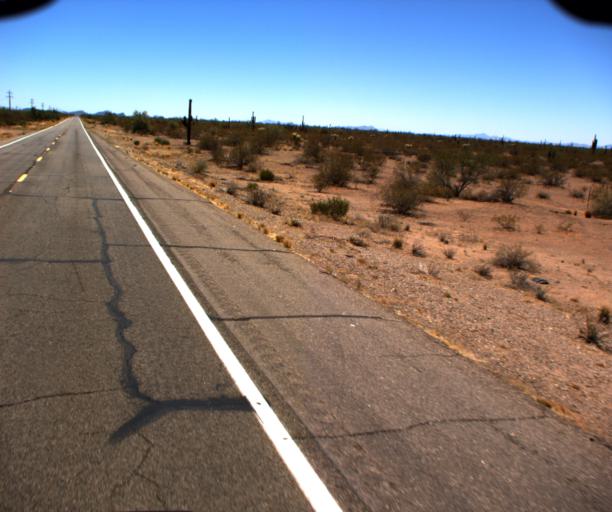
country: US
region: Arizona
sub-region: Pima County
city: Sells
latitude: 32.0885
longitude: -112.0562
